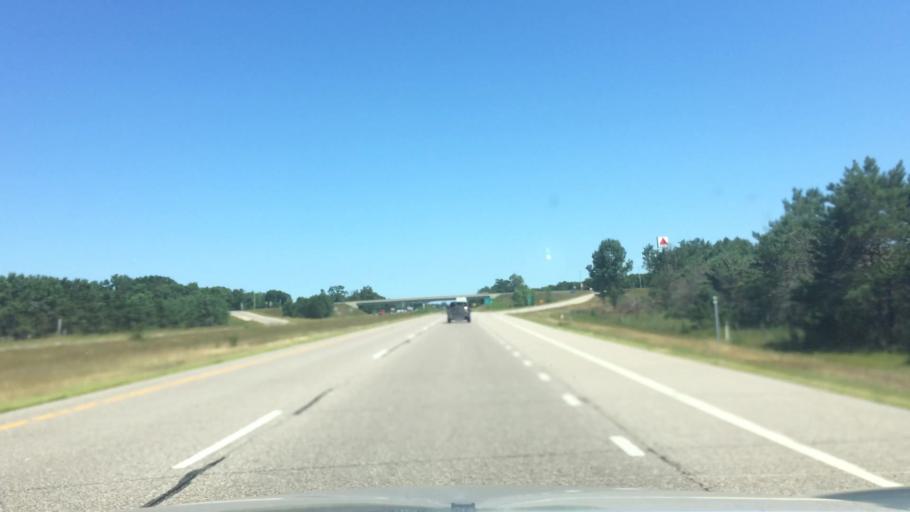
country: US
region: Wisconsin
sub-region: Marquette County
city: Westfield
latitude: 44.1300
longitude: -89.5323
